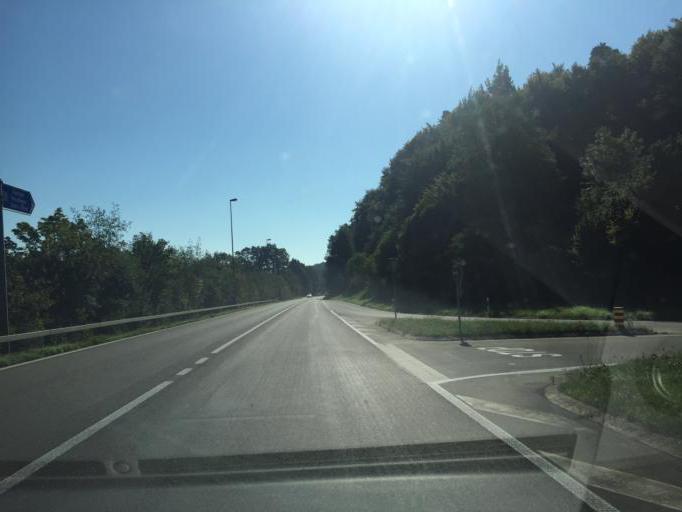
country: DE
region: Baden-Wuerttemberg
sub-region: Freiburg Region
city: Gailingen
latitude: 47.6772
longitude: 8.7770
